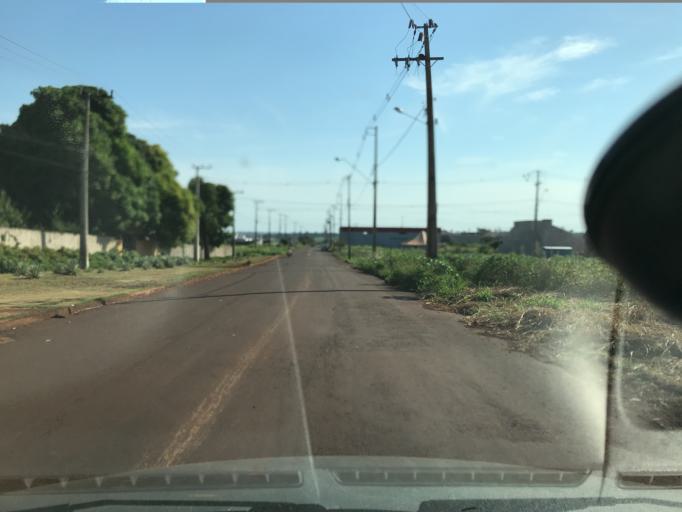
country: BR
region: Parana
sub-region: Palotina
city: Palotina
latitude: -24.2945
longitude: -53.8299
